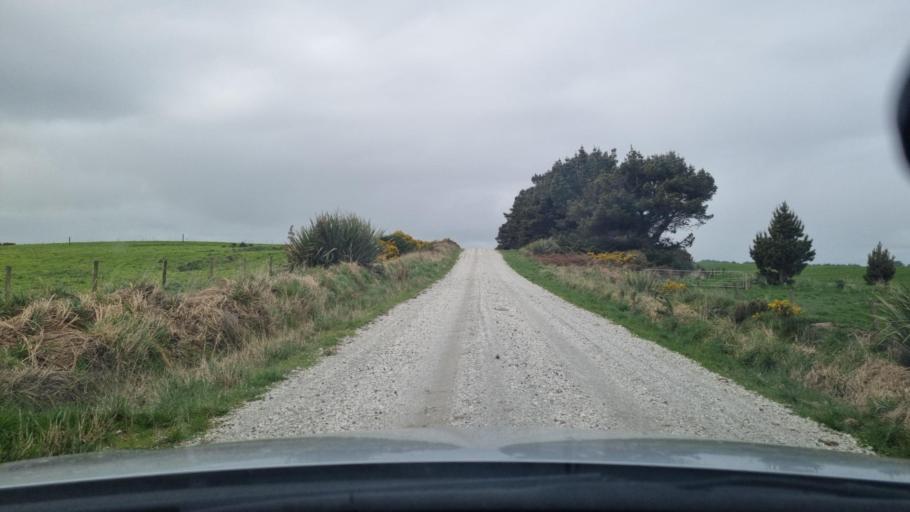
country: NZ
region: Southland
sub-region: Invercargill City
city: Invercargill
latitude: -46.5016
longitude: 168.4067
